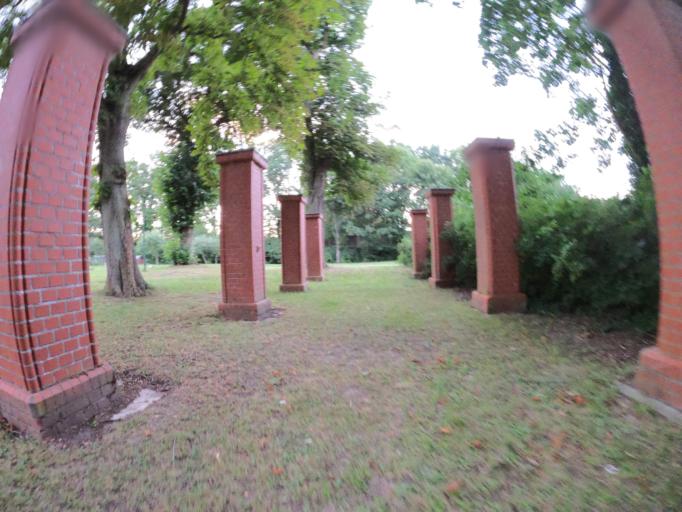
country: DE
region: Mecklenburg-Vorpommern
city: Woldegk
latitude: 53.4582
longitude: 13.5869
